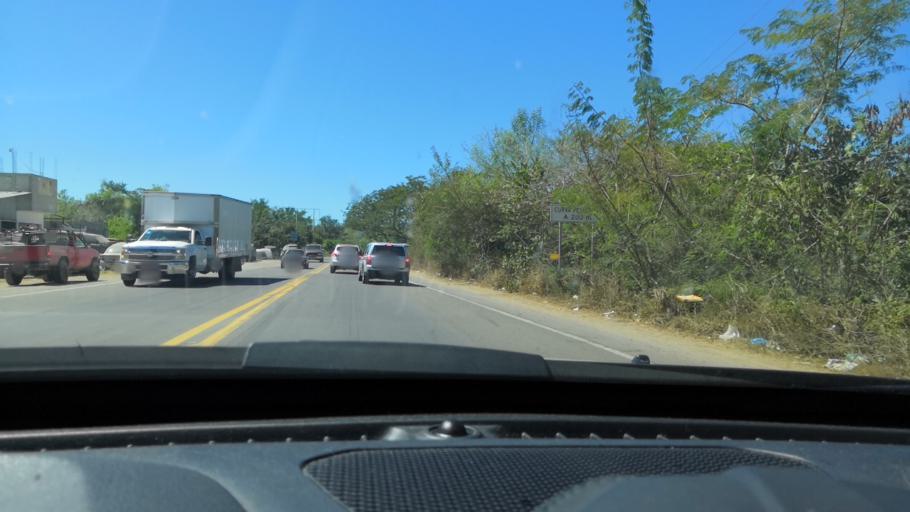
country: MX
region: Nayarit
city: Las Varas
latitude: 21.1728
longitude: -105.1469
